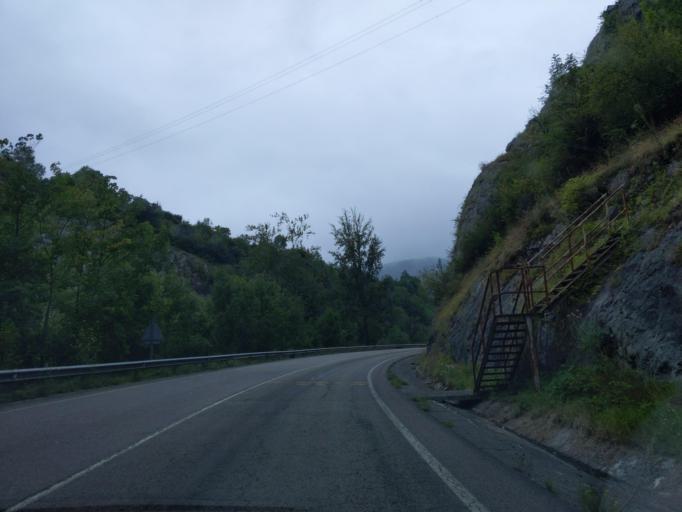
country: ES
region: Asturias
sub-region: Province of Asturias
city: Pola de Laviana
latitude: 43.2319
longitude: -5.4939
